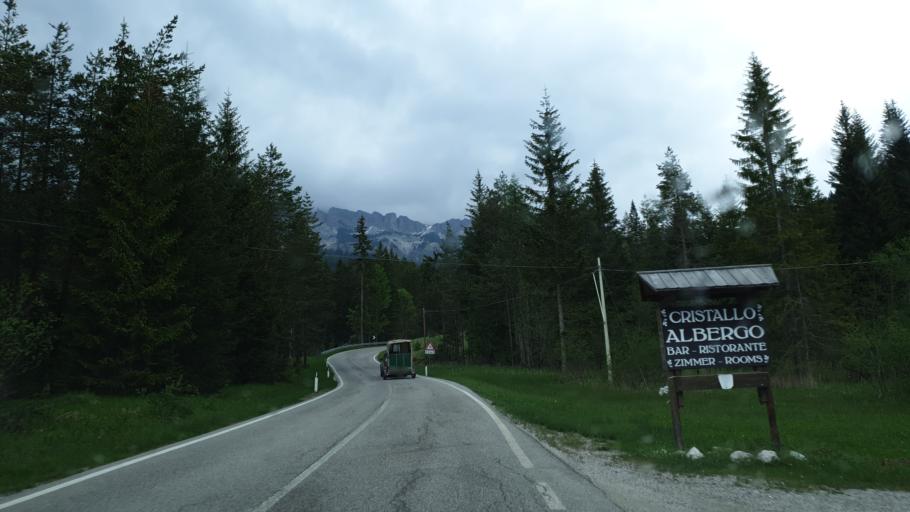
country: IT
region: Veneto
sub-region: Provincia di Belluno
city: San Vito
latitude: 46.5470
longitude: 12.2485
